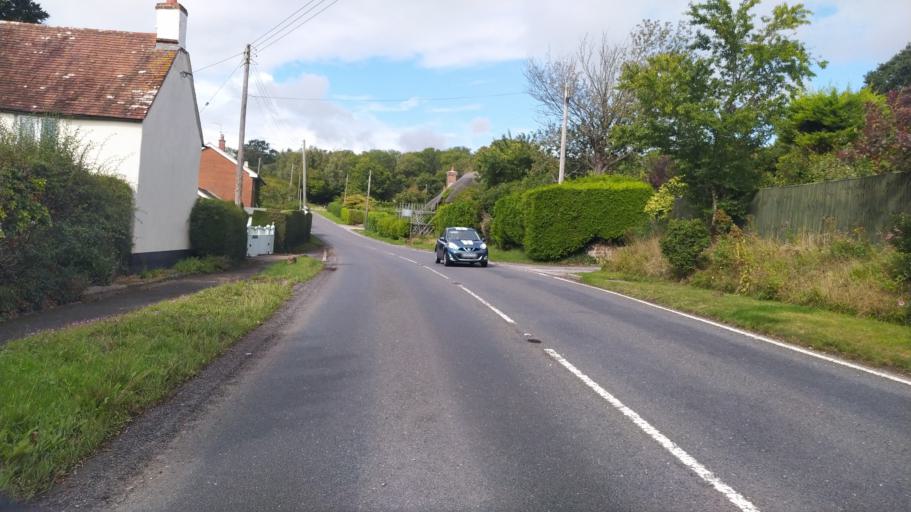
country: GB
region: England
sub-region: Dorset
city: Blandford Forum
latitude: 50.8430
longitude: -2.1014
